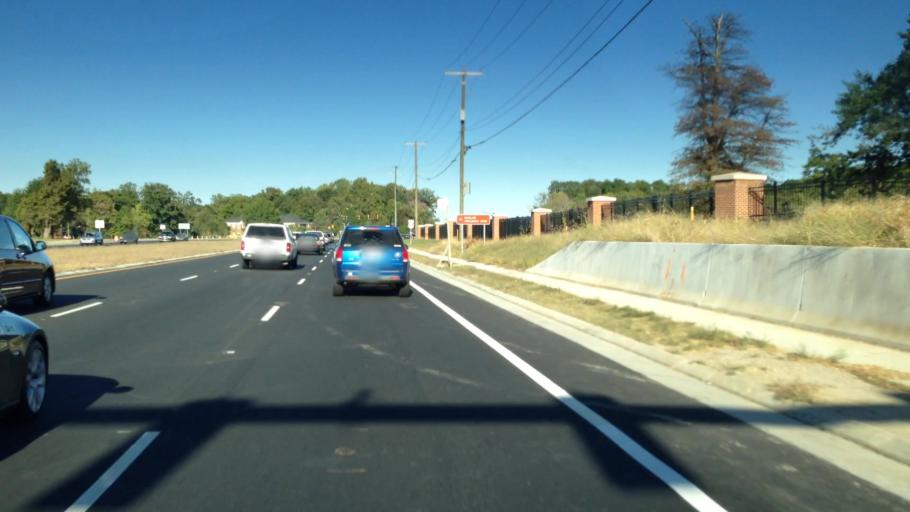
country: US
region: Virginia
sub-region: Fairfax County
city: Fort Belvoir
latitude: 38.7116
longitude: -77.1432
